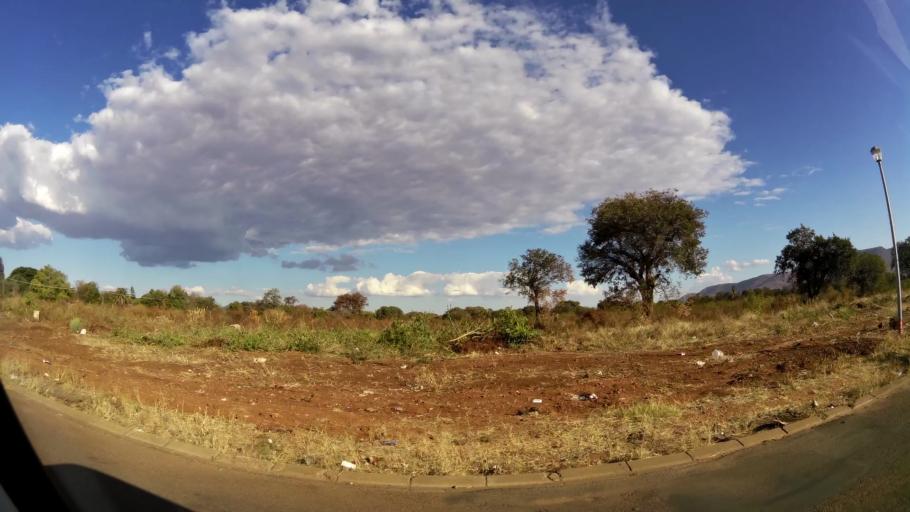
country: ZA
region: Limpopo
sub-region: Waterberg District Municipality
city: Mokopane
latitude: -24.1819
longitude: 28.9964
